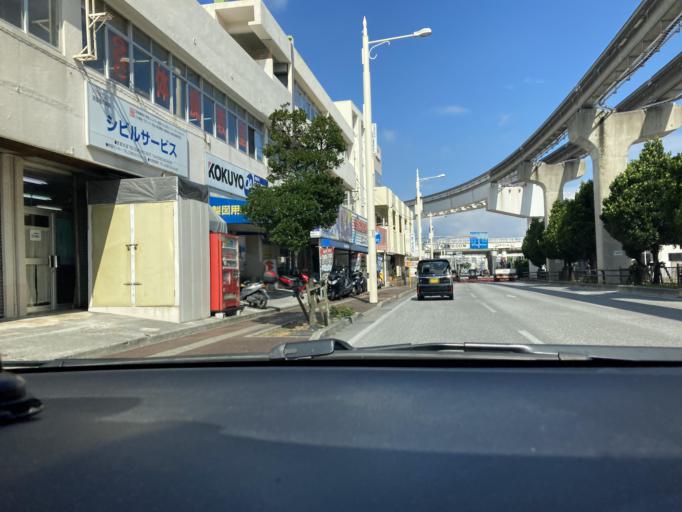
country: JP
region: Okinawa
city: Naha-shi
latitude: 26.2310
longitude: 127.7052
